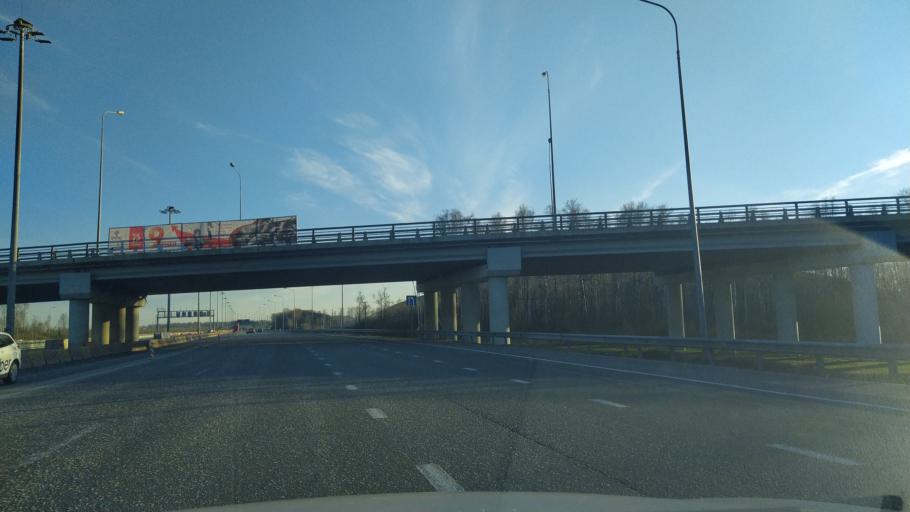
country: RU
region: St.-Petersburg
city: Levashovo
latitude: 60.0755
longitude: 30.1810
